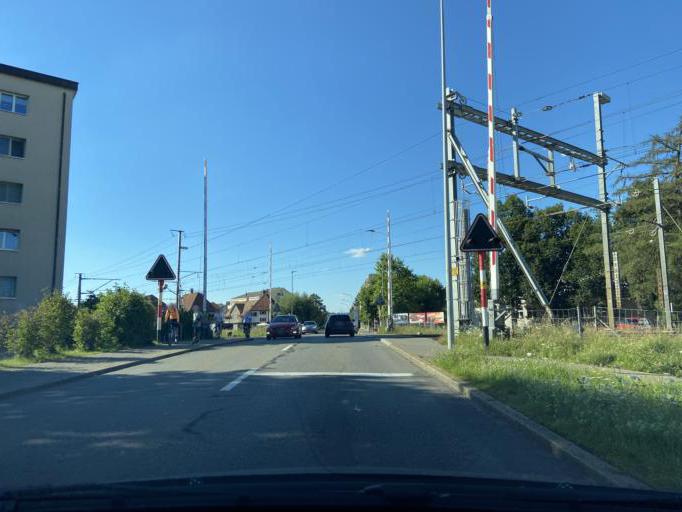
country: CH
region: Zurich
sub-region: Bezirk Uster
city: Uster / Gschwader
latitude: 47.3535
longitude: 8.7130
